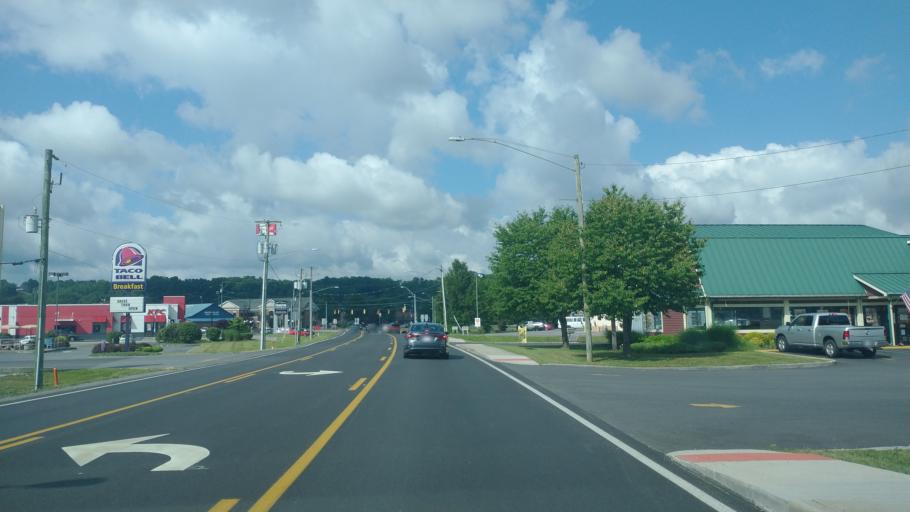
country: US
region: West Virginia
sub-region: Mercer County
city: Princeton
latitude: 37.3625
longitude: -81.0966
